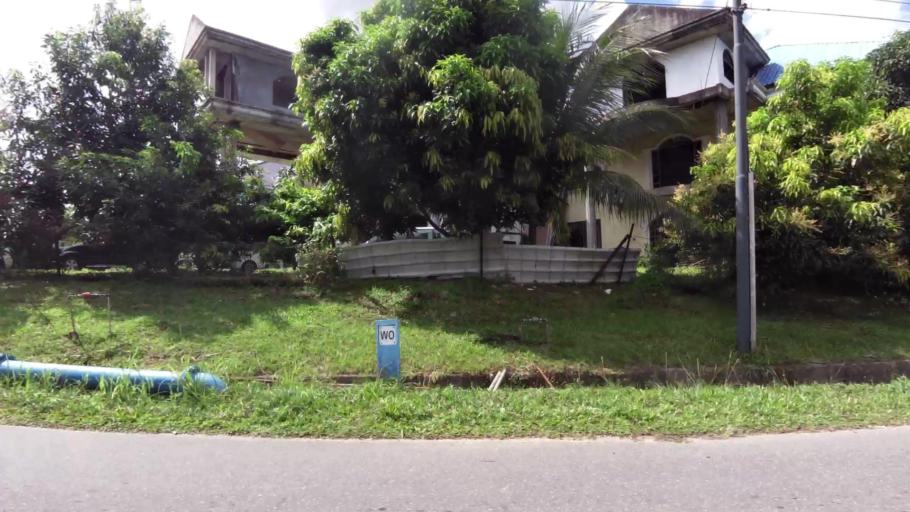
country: BN
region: Brunei and Muara
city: Bandar Seri Begawan
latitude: 4.9569
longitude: 114.9559
